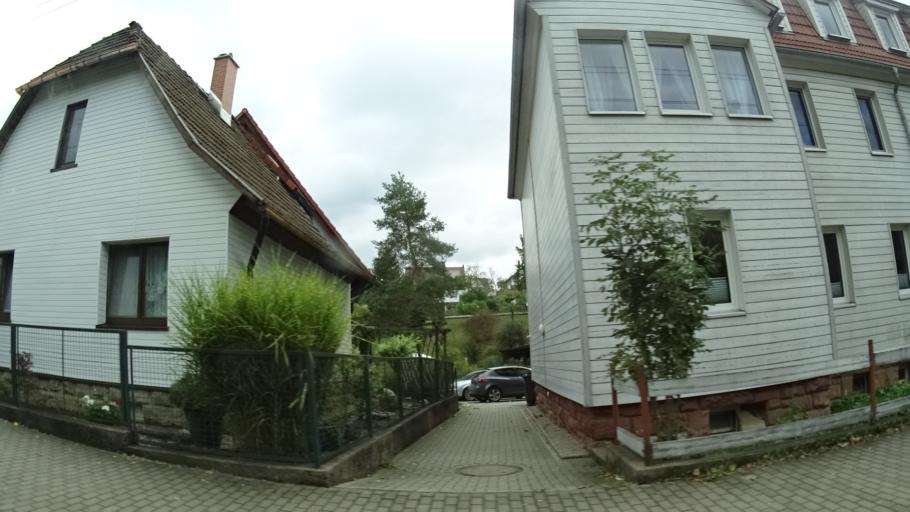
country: DE
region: Thuringia
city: Schmalkalden
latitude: 50.7168
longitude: 10.4699
